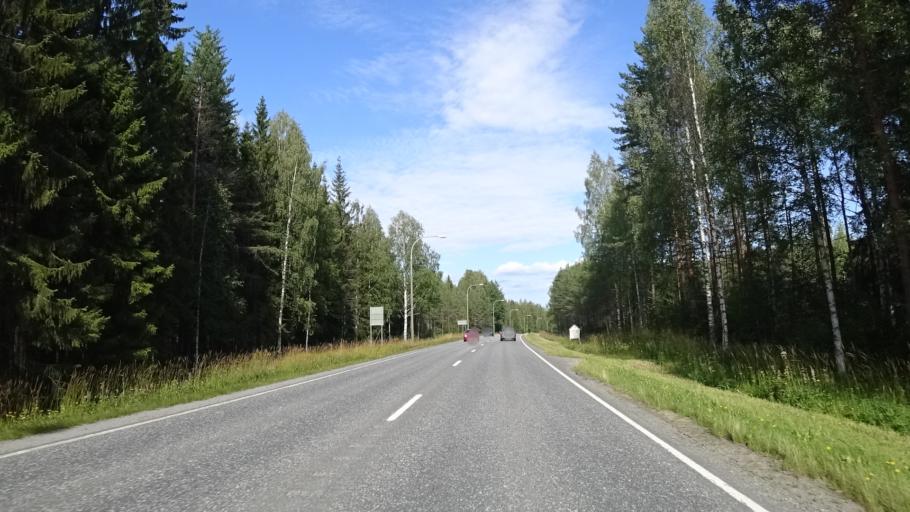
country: FI
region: North Karelia
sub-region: Joensuu
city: Eno
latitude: 62.7948
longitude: 30.0911
